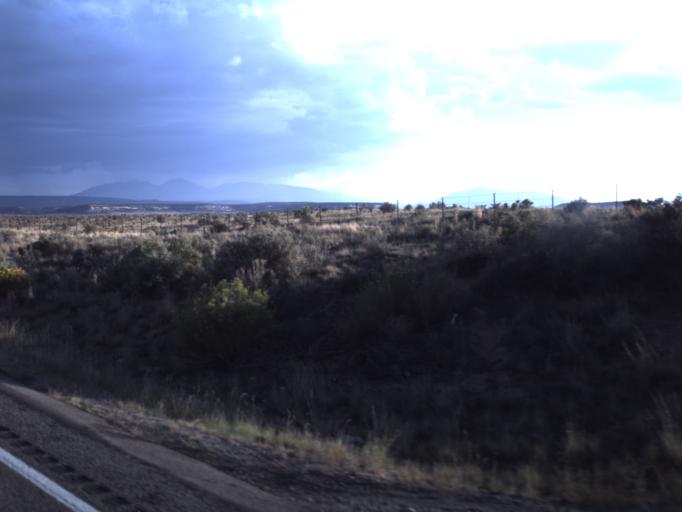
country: US
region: Utah
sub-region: San Juan County
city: Monticello
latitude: 38.1342
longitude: -109.3700
